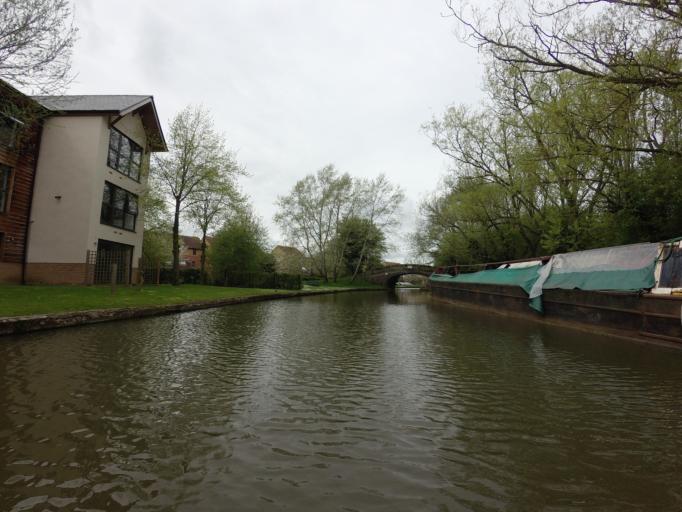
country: GB
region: England
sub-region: Milton Keynes
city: Simpson
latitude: 52.0263
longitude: -0.7292
